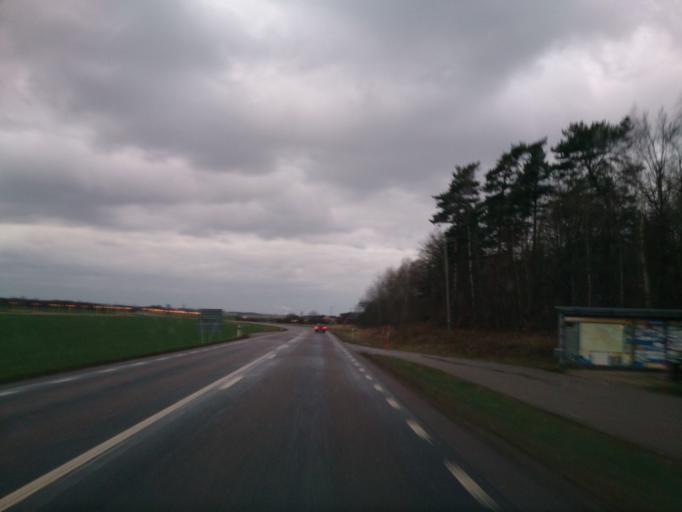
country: SE
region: OEstergoetland
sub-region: Linkopings Kommun
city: Sturefors
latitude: 58.3999
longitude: 15.7177
